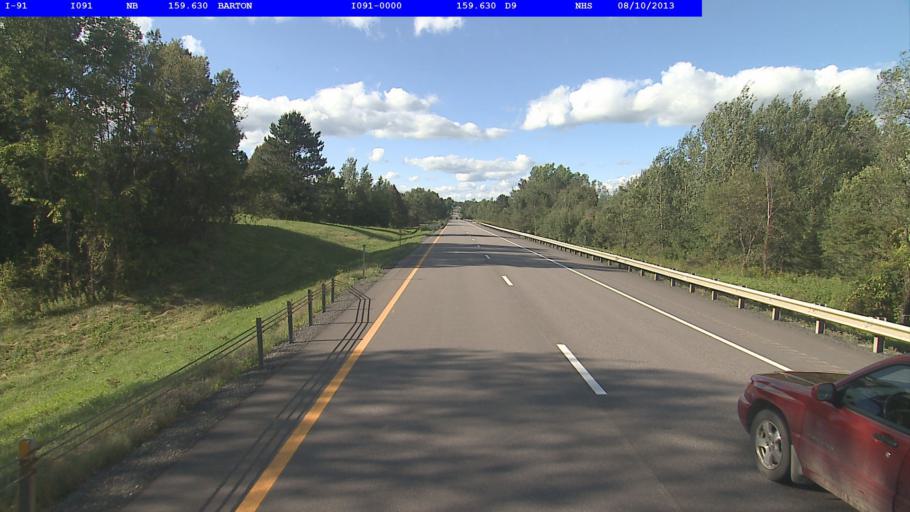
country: US
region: Vermont
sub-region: Orleans County
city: Newport
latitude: 44.7810
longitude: -72.2150
